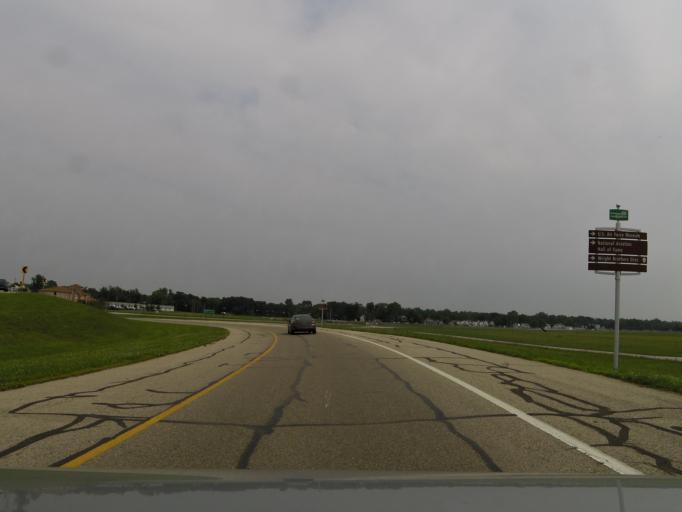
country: US
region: Ohio
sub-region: Montgomery County
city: Riverside
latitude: 39.7814
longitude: -84.1164
